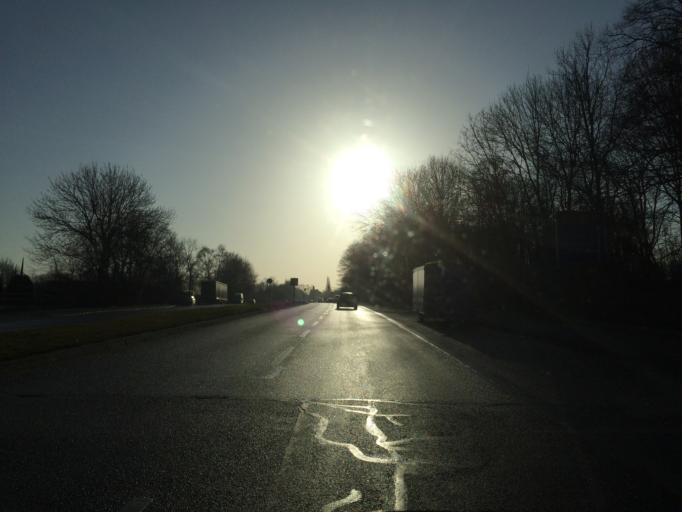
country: DE
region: North Rhine-Westphalia
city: Bochum-Hordel
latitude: 51.5417
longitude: 7.1700
